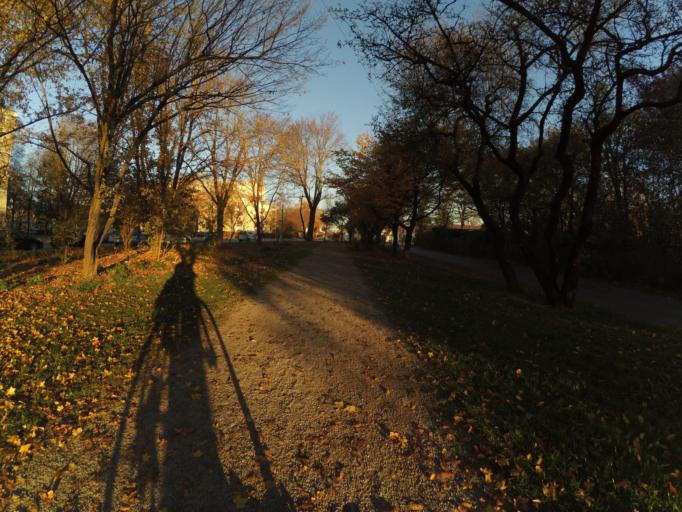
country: DE
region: Bavaria
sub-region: Upper Bavaria
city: Oberschleissheim
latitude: 48.2041
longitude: 11.5512
